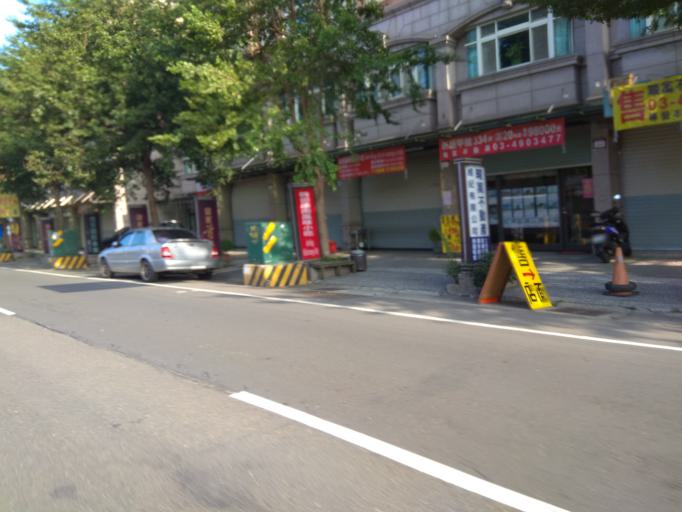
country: TW
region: Taiwan
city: Taoyuan City
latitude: 24.9642
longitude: 121.1529
